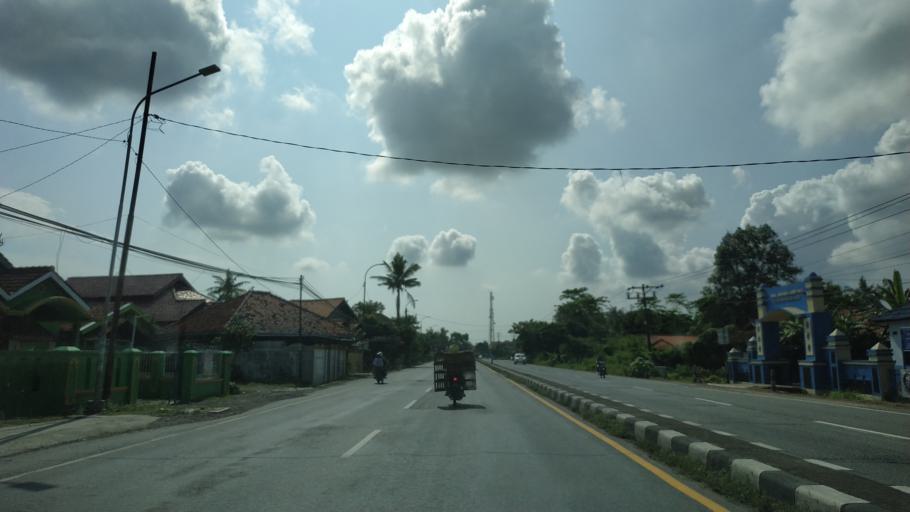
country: ID
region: Central Java
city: Comal
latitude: -6.8847
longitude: 109.5598
